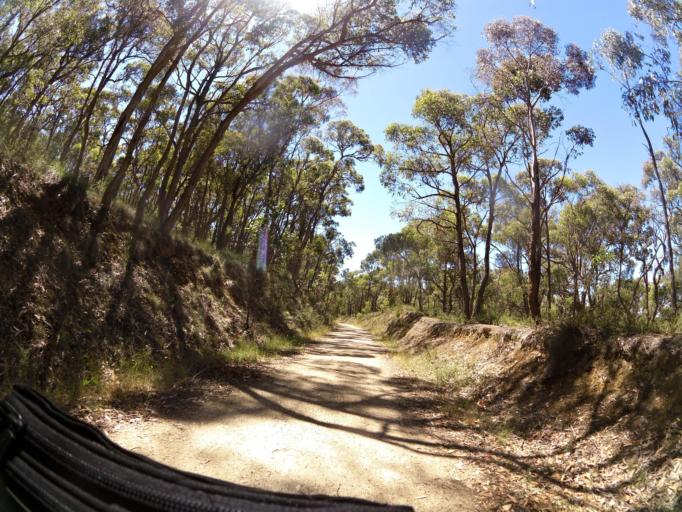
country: AU
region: Victoria
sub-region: Ballarat North
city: Delacombe
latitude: -37.7101
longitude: 143.6157
